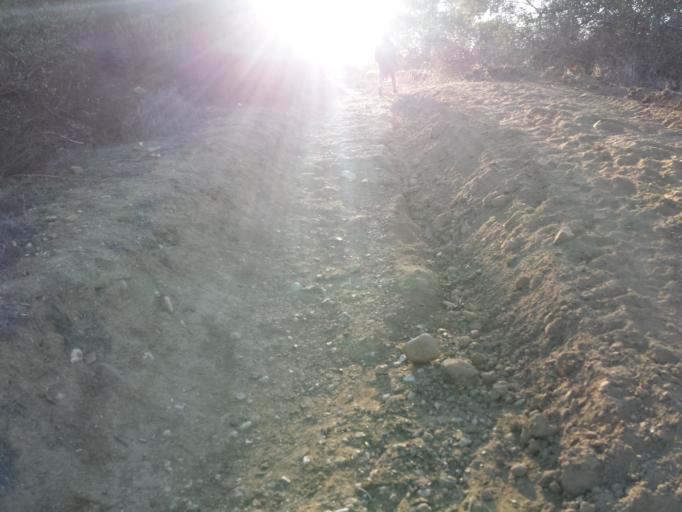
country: US
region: California
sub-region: Los Angeles County
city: Whittier
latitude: 34.0021
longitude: -118.0083
